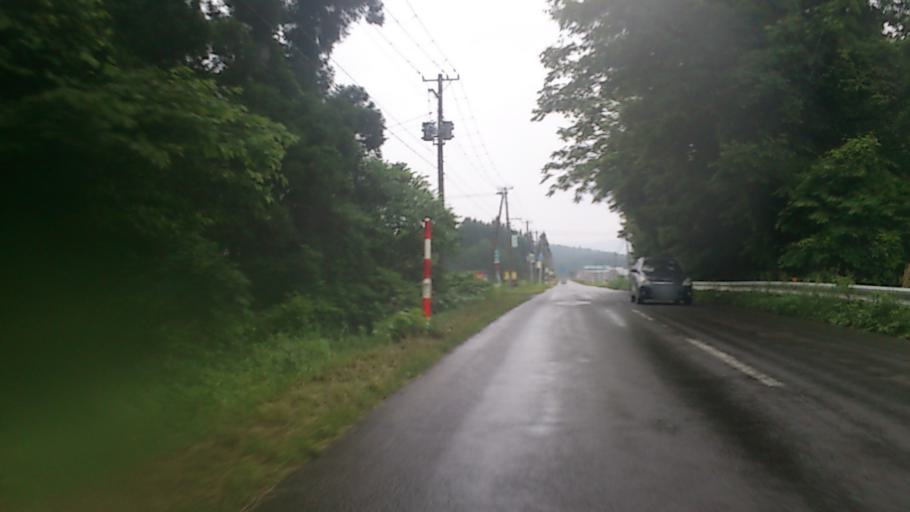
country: JP
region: Akita
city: Takanosu
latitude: 40.2485
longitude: 140.2511
